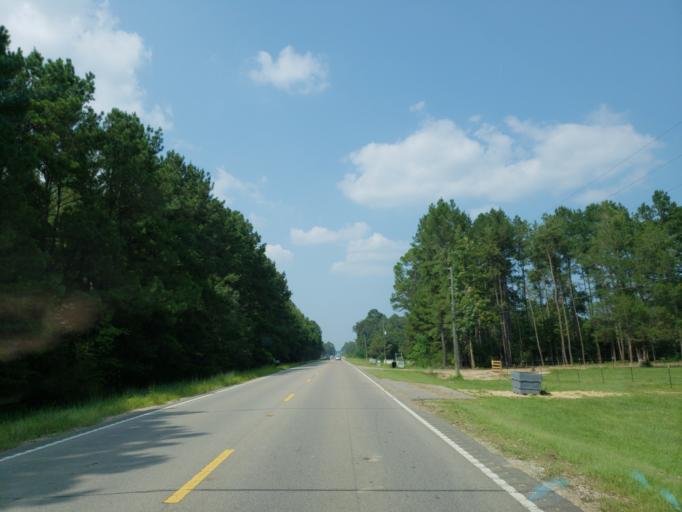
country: US
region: Mississippi
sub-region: Forrest County
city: Glendale
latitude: 31.4604
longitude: -89.2846
